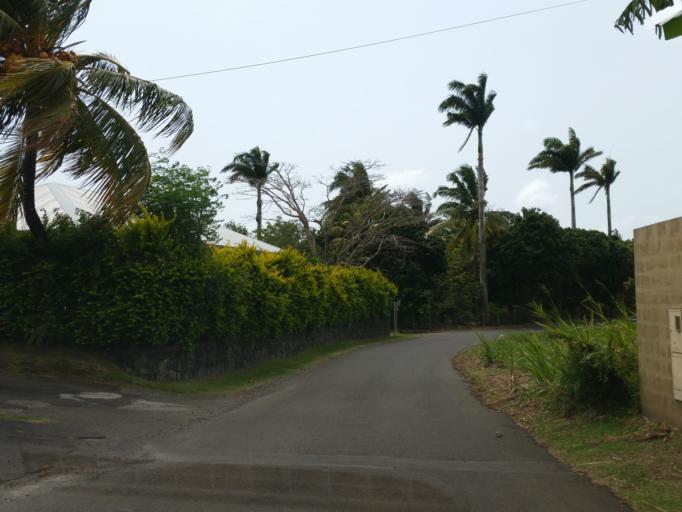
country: RE
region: Reunion
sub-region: Reunion
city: Sainte-Suzanne
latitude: -20.9175
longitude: 55.6131
